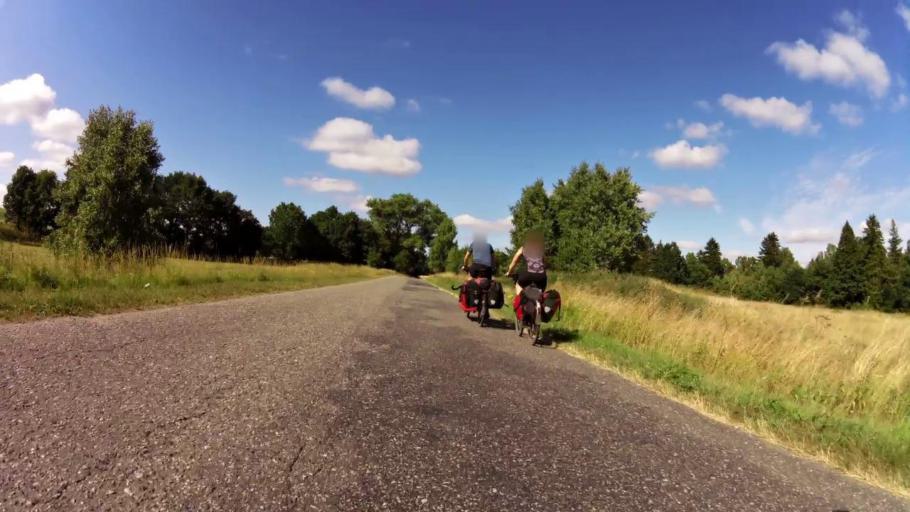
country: PL
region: West Pomeranian Voivodeship
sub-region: Powiat lobeski
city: Lobez
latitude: 53.6511
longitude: 15.6756
